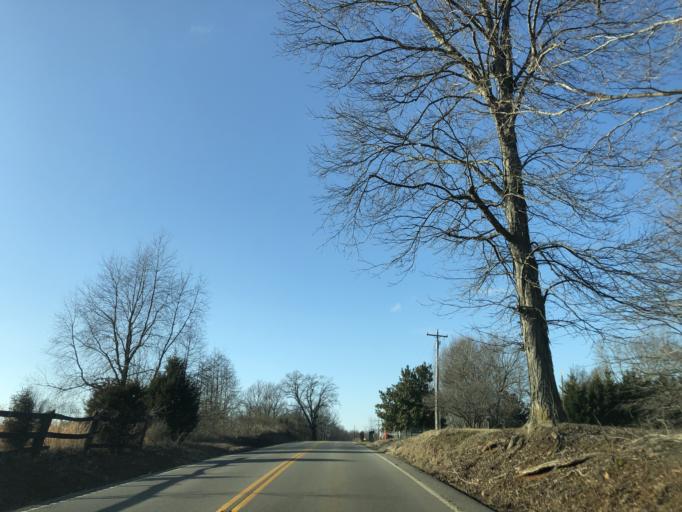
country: US
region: Tennessee
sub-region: Sumner County
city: White House
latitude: 36.4917
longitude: -86.5886
